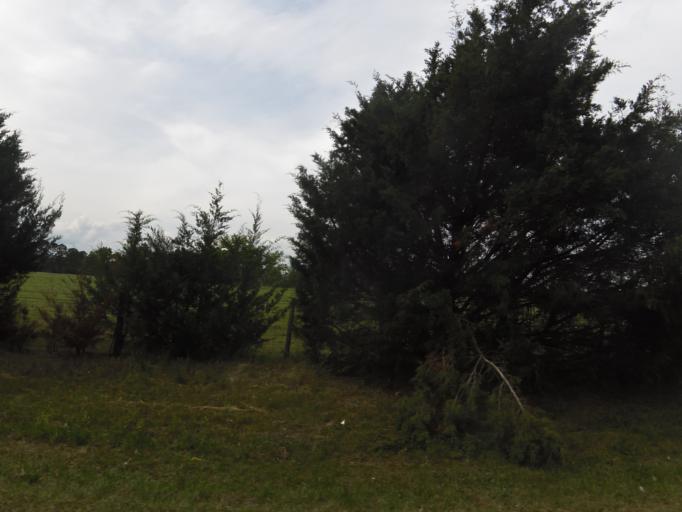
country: US
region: Georgia
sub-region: McDuffie County
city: Thomson
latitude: 33.5232
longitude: -82.4495
